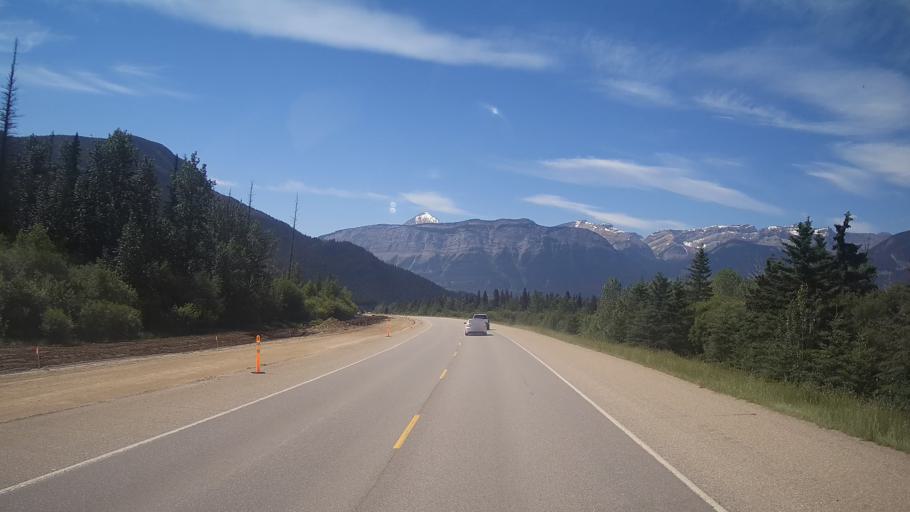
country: CA
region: Alberta
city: Jasper Park Lodge
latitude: 53.0651
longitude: -118.0638
